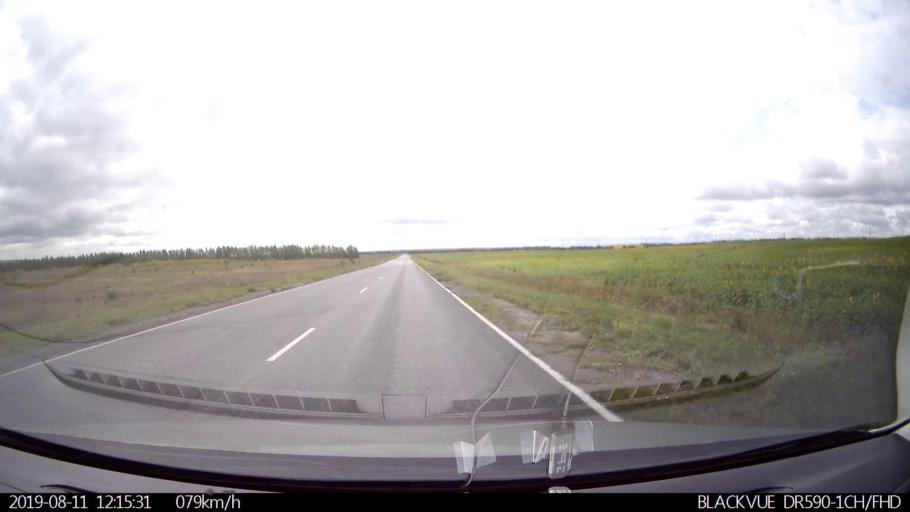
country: RU
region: Ulyanovsk
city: Ignatovka
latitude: 53.9409
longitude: 47.9678
